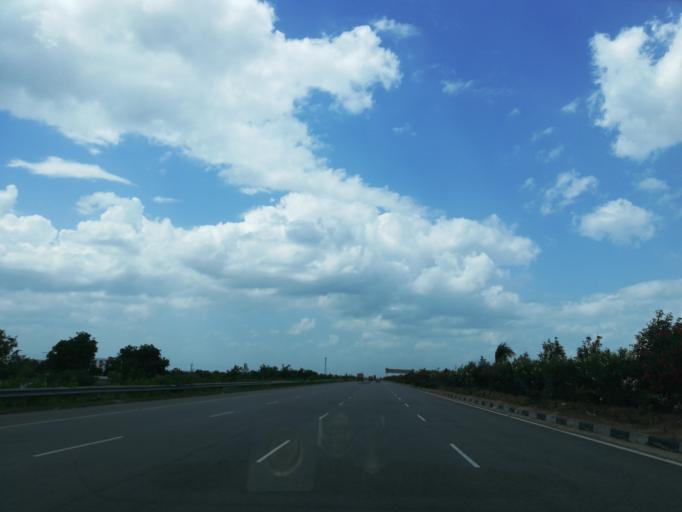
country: IN
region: Telangana
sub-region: Medak
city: Patancheru
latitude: 17.4801
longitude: 78.2468
